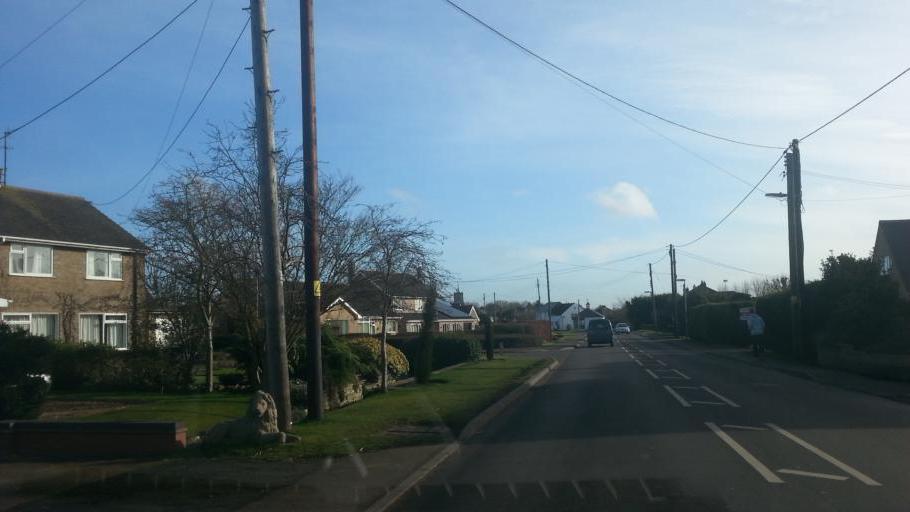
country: GB
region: England
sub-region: Cambridgeshire
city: Somersham
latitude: 52.3821
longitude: -0.0103
